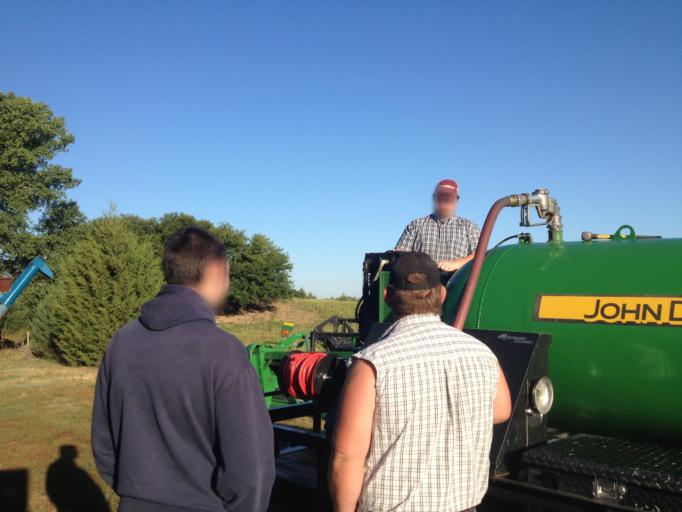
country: US
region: Kansas
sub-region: Barton County
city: Great Bend
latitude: 38.3243
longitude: -98.7233
